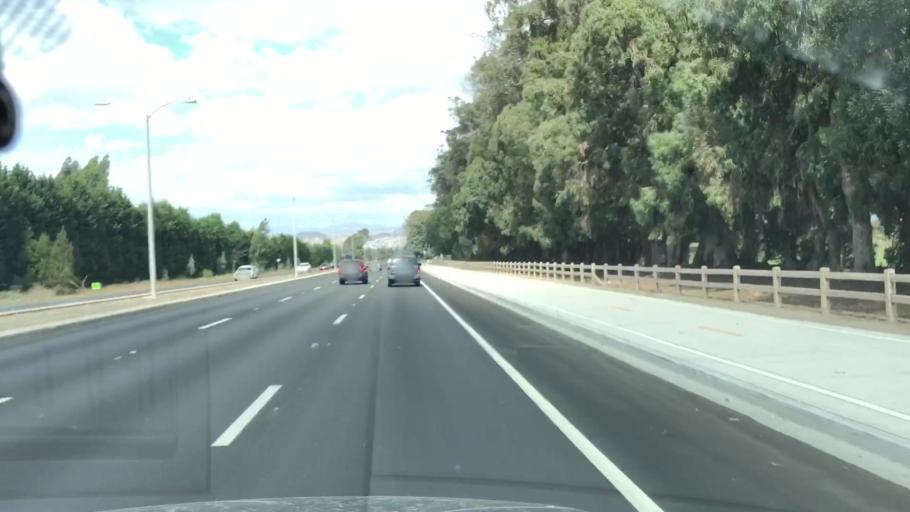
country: US
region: California
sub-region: Ventura County
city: Oxnard Shores
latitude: 34.2214
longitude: -119.2210
